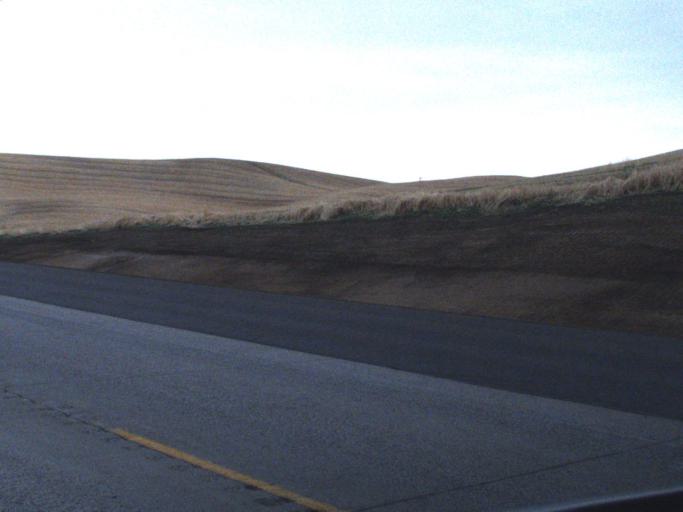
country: US
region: Washington
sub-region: Whitman County
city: Colfax
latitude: 46.9836
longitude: -117.3455
